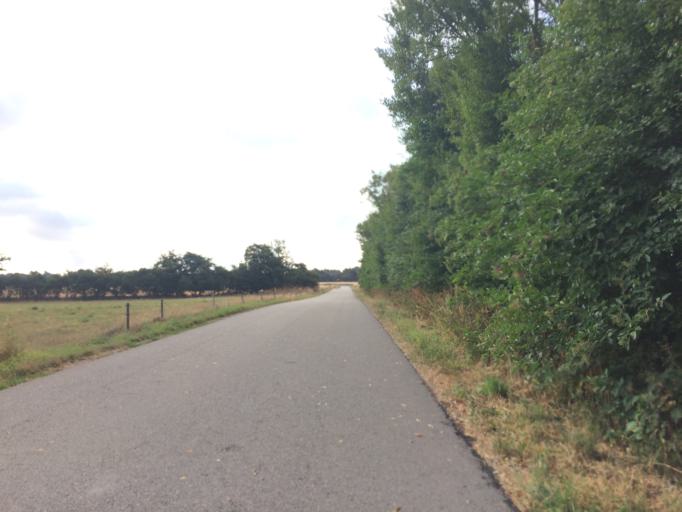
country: DK
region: Central Jutland
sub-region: Holstebro Kommune
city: Vinderup
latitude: 56.6085
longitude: 8.7854
